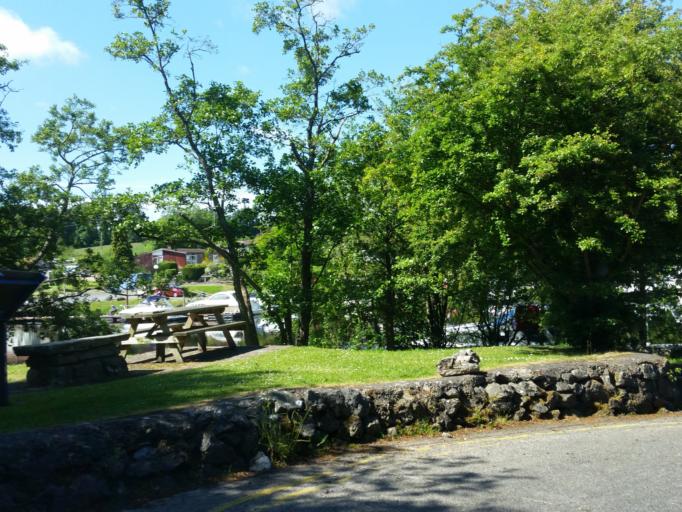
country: GB
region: Northern Ireland
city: Lisnaskea
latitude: 54.2855
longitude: -7.5473
